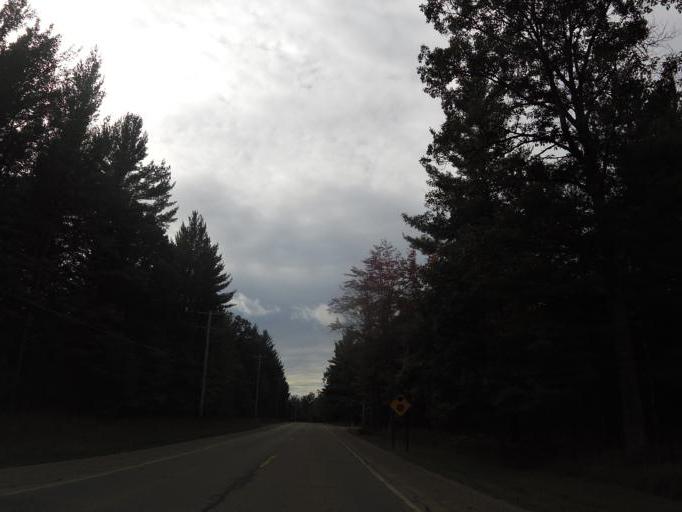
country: US
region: Michigan
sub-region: Roscommon County
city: Saint Helen
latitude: 44.3491
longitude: -84.4879
